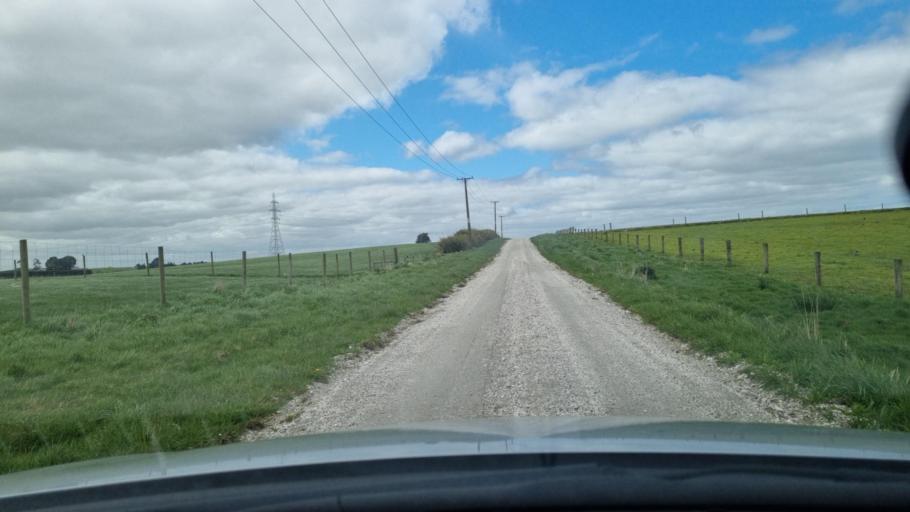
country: NZ
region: Southland
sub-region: Invercargill City
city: Invercargill
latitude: -46.4430
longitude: 168.4468
